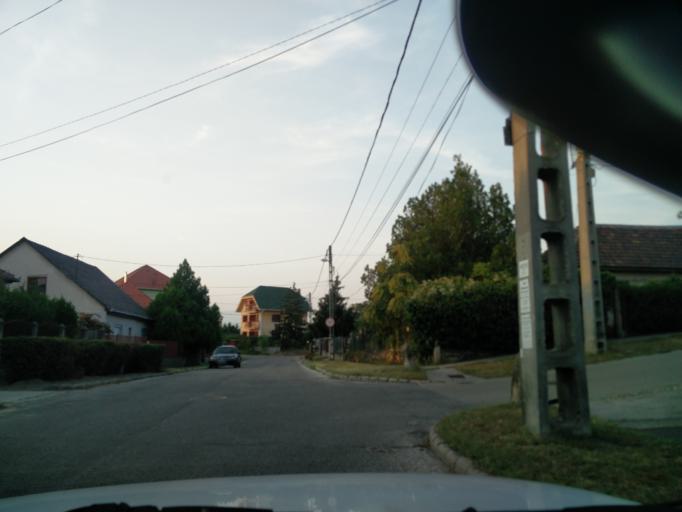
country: HU
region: Budapest
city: Budapest XXI. keruelet
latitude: 47.4084
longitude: 19.0856
